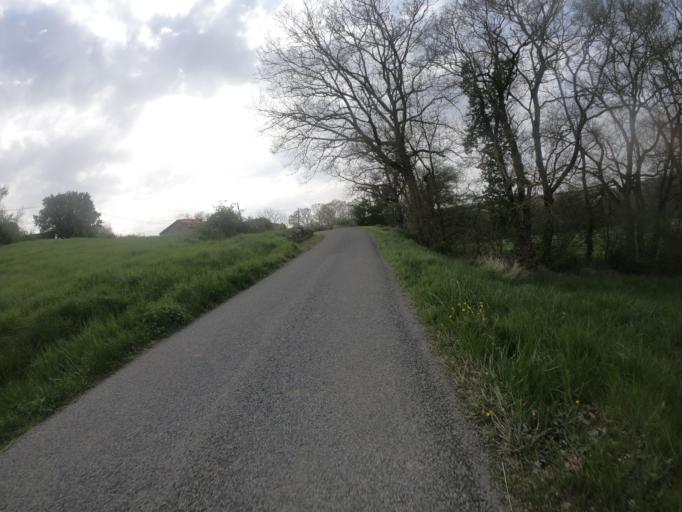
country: FR
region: Languedoc-Roussillon
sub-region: Departement de l'Aude
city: Belpech
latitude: 43.1247
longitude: 1.7421
